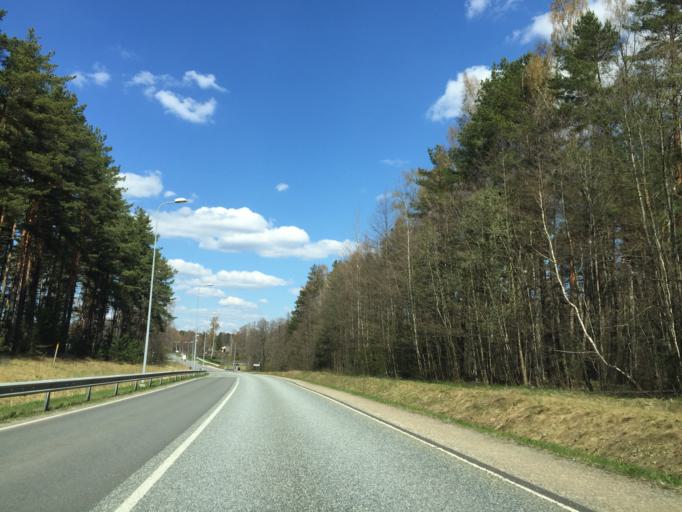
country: LV
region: Saulkrastu
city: Saulkrasti
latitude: 57.2274
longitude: 24.3929
